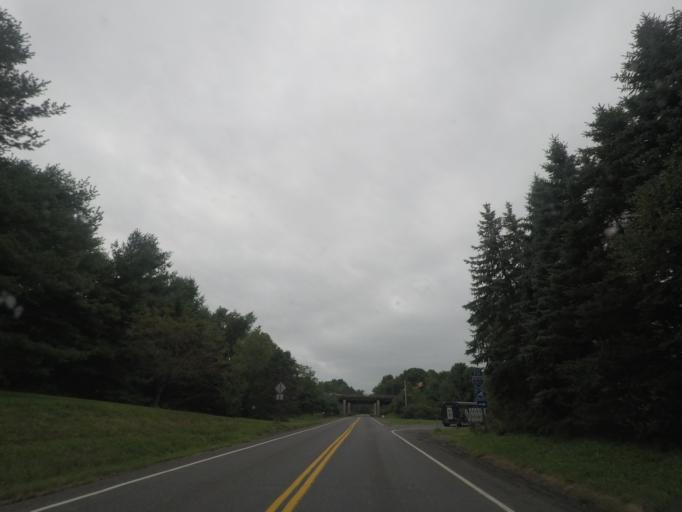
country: US
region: New York
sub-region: Columbia County
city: Chatham
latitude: 42.4063
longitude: -73.5470
